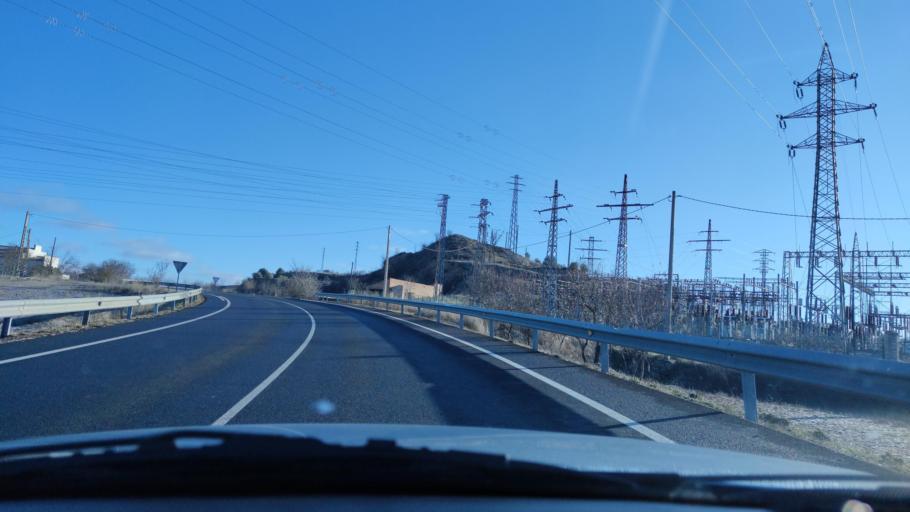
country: ES
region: Catalonia
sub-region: Provincia de Lleida
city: Cervera
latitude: 41.6808
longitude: 1.2900
